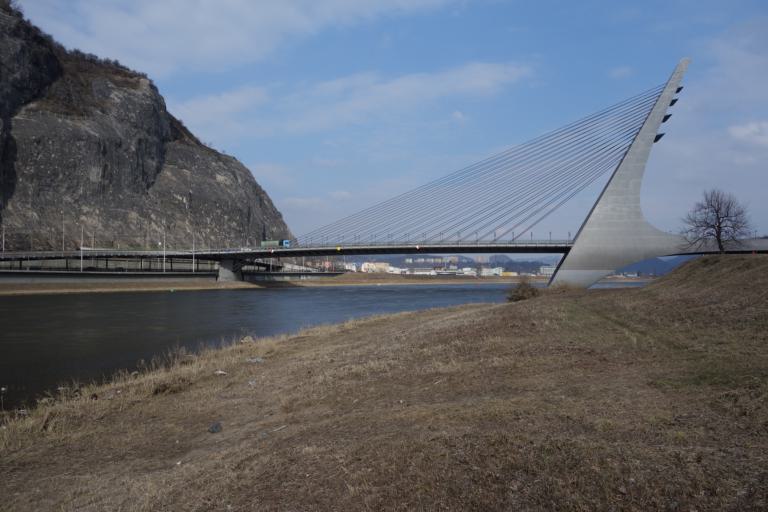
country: CZ
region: Ustecky
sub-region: Okres Usti nad Labem
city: Usti nad Labem
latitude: 50.6595
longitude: 14.0507
